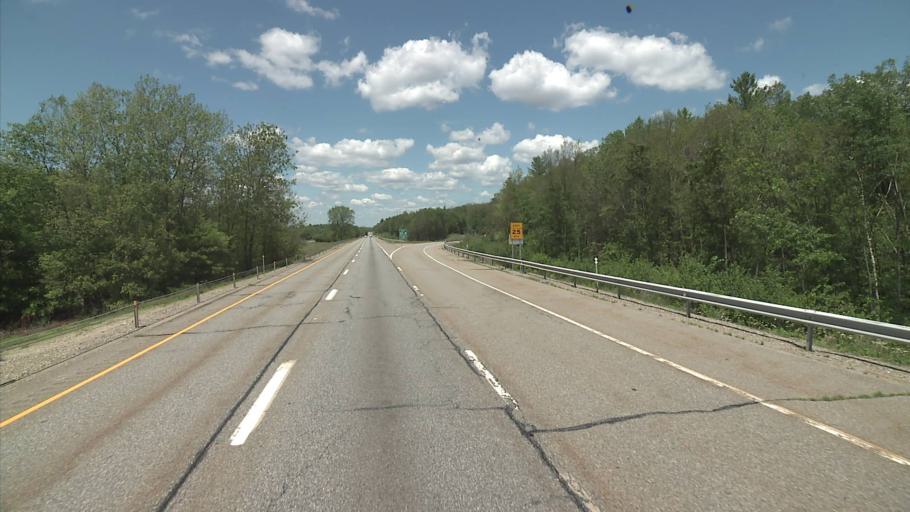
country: US
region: Connecticut
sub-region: Windham County
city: Thompson
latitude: 42.0055
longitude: -71.8534
